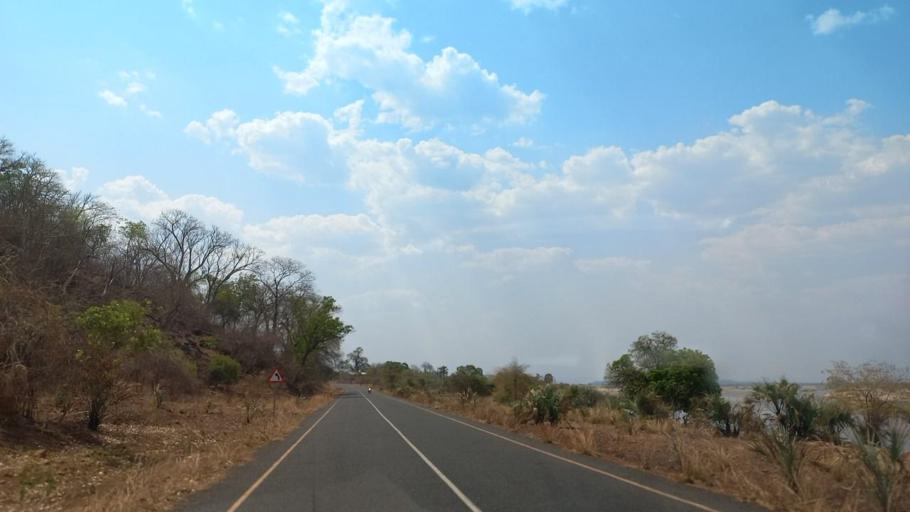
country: ZM
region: Lusaka
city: Luangwa
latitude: -15.3114
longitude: 30.3261
